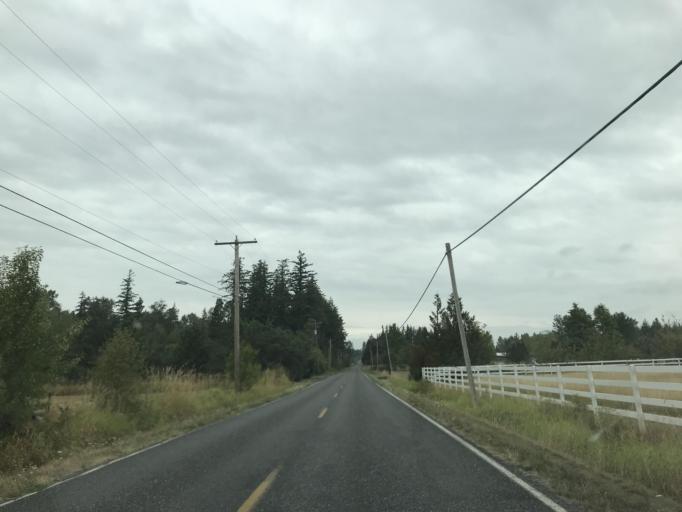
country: US
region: Washington
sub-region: Whatcom County
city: Sudden Valley
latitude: 48.8212
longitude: -122.3325
